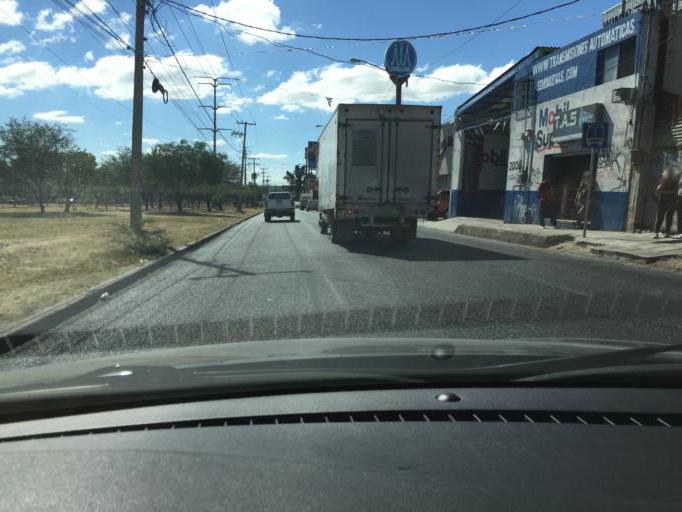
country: MX
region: Guanajuato
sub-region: Leon
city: Ejido la Joya
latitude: 21.1050
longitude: -101.7116
